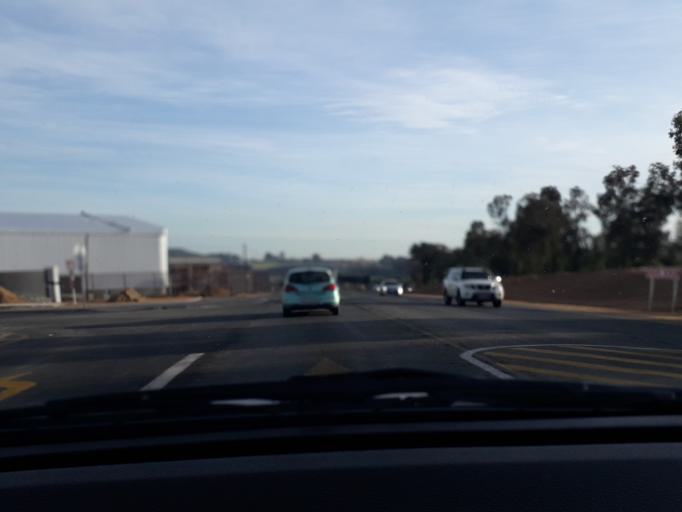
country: ZA
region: Gauteng
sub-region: City of Tshwane Metropolitan Municipality
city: Centurion
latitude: -25.9207
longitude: 28.1538
